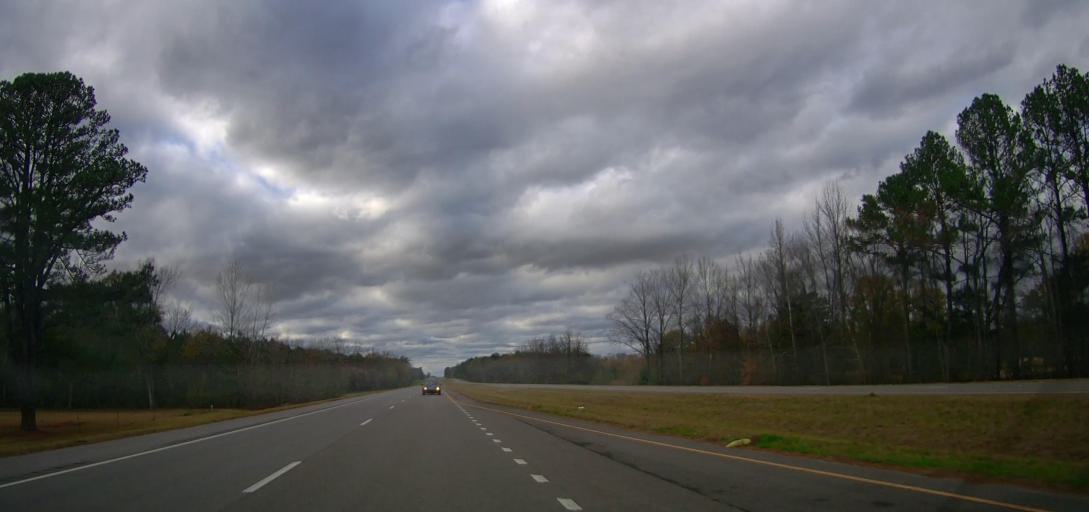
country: US
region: Alabama
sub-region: Morgan County
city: Danville
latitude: 34.3476
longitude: -87.0388
